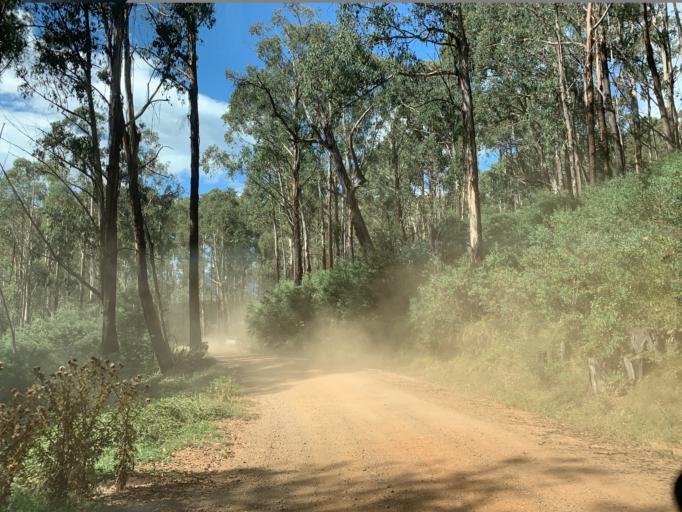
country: AU
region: Victoria
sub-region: Mansfield
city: Mansfield
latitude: -37.0955
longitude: 146.5401
